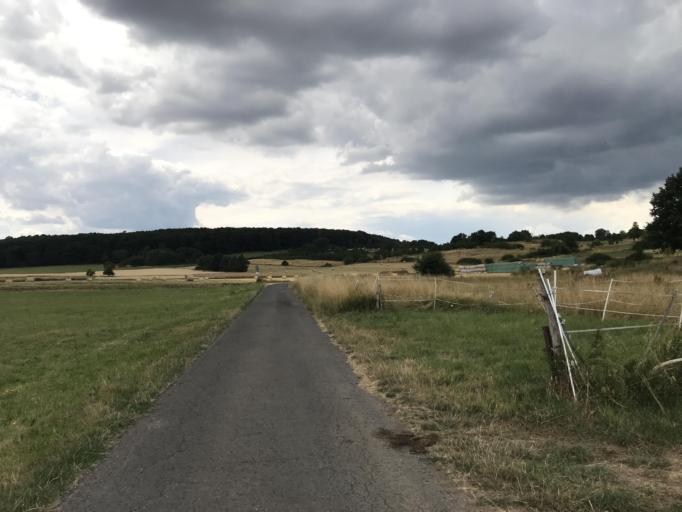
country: DE
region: Hesse
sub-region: Regierungsbezirk Giessen
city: Reiskirchen
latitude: 50.5852
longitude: 8.8564
